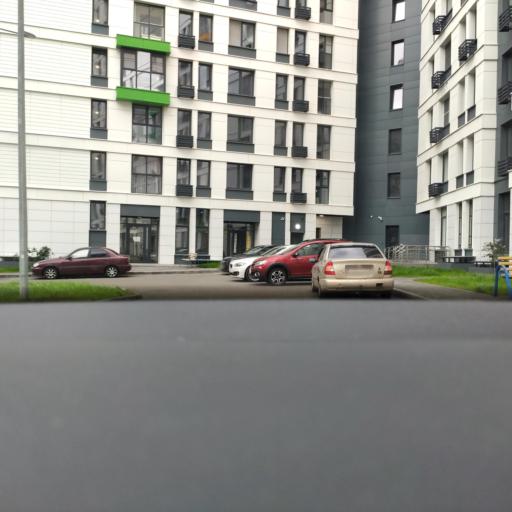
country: RU
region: Moscow
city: Severnyy
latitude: 55.9208
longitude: 37.5558
